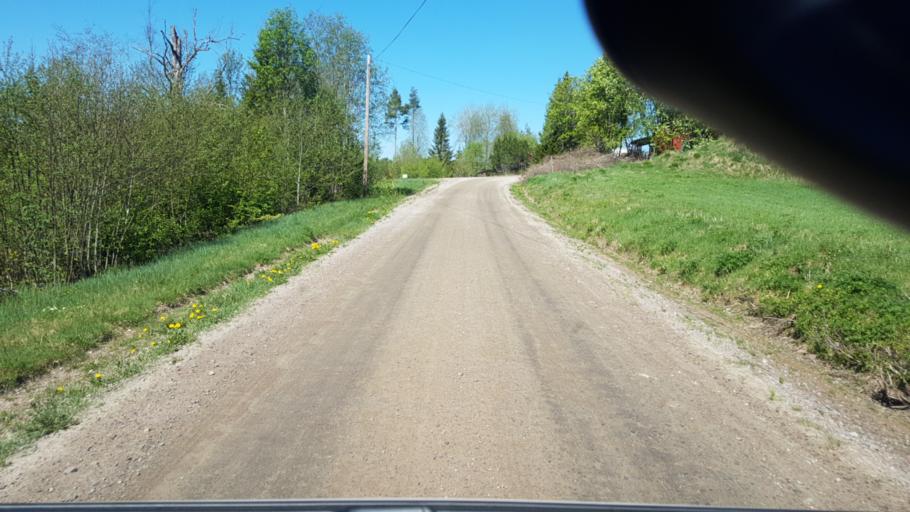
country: SE
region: Vaermland
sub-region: Arvika Kommun
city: Arvika
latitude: 59.8680
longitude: 12.6166
